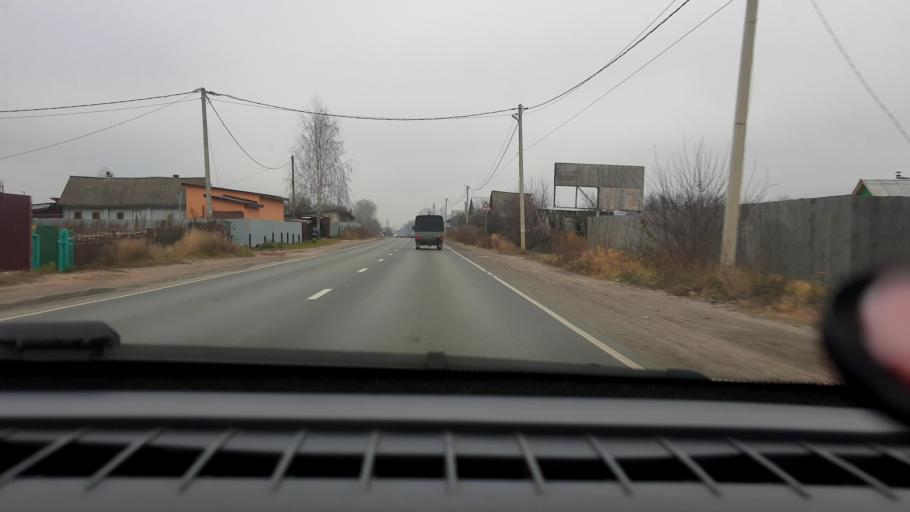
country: RU
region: Nizjnij Novgorod
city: Gidrotorf
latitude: 56.5452
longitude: 43.5273
